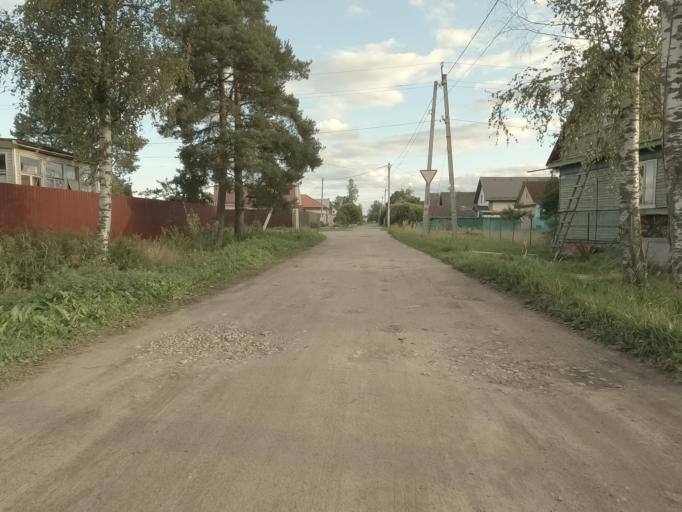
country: RU
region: Leningrad
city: Mga
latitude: 59.7610
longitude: 31.0742
